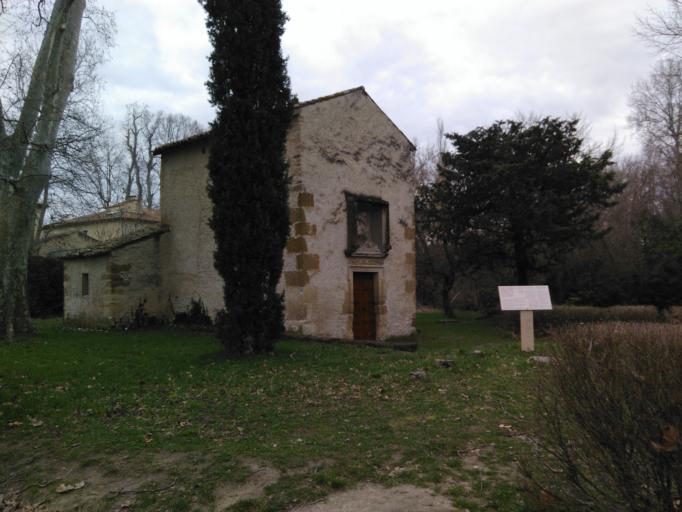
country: FR
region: Provence-Alpes-Cote d'Azur
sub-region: Departement du Vaucluse
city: Aubignan
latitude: 44.0880
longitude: 5.0535
